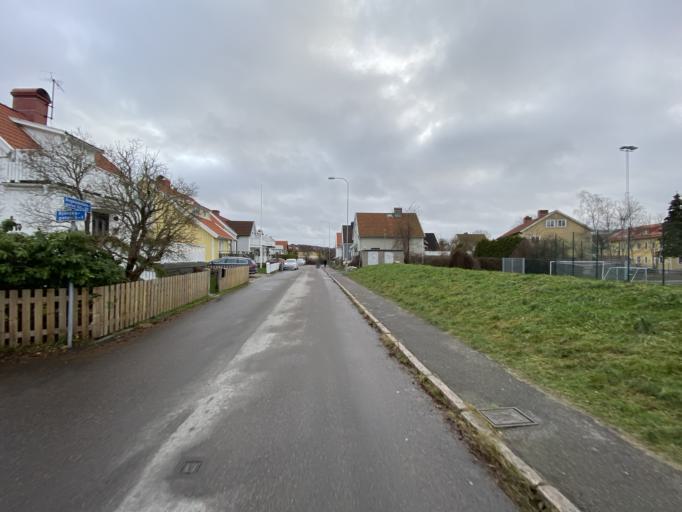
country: SE
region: Vaestra Goetaland
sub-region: Goteborg
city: Goeteborg
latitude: 57.7166
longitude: 12.0201
